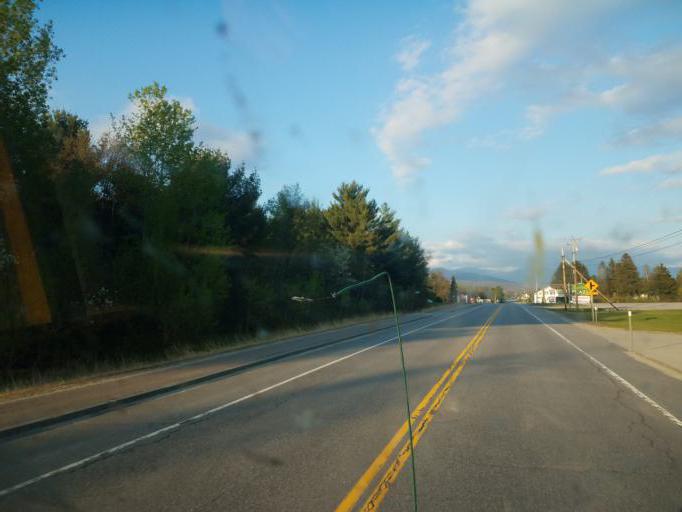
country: US
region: New Hampshire
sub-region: Grafton County
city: Deerfield
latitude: 44.2667
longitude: -71.5629
